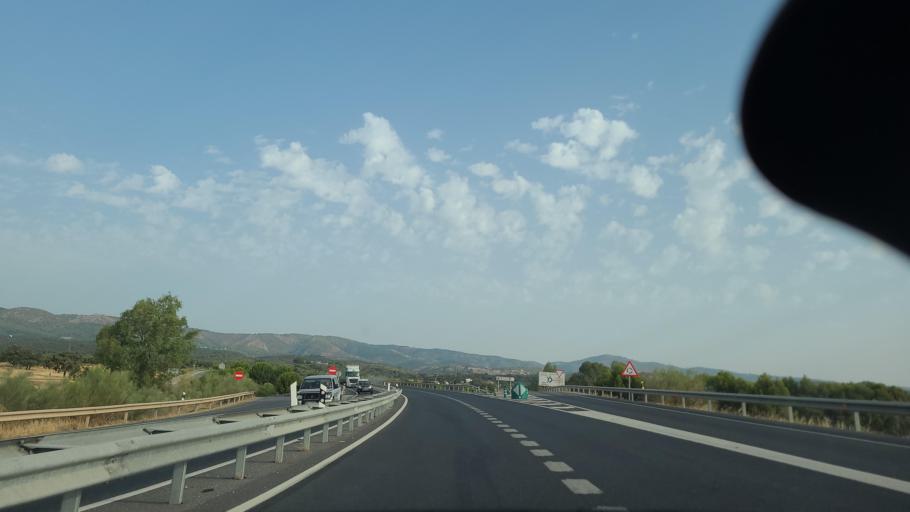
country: ES
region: Andalusia
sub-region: Province of Cordoba
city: Cordoba
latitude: 37.9174
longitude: -4.7601
